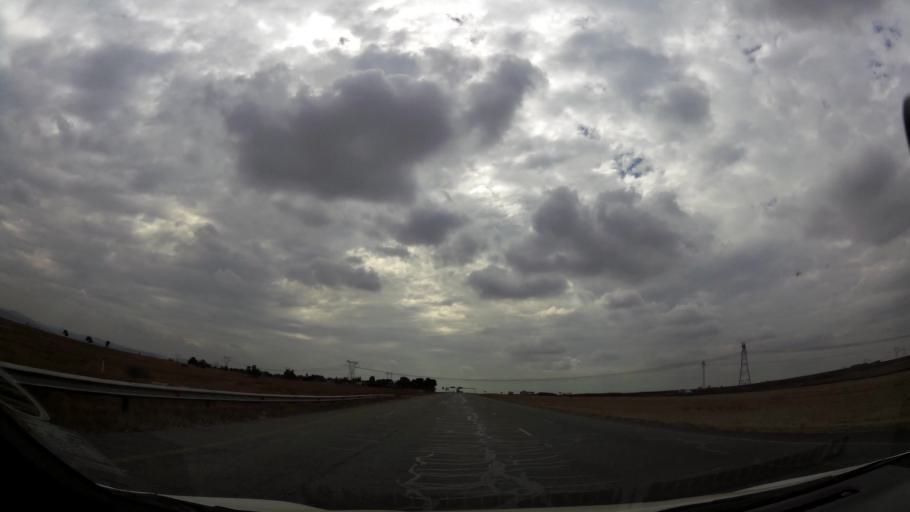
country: ZA
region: Gauteng
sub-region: Ekurhuleni Metropolitan Municipality
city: Germiston
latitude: -26.3617
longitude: 28.0954
